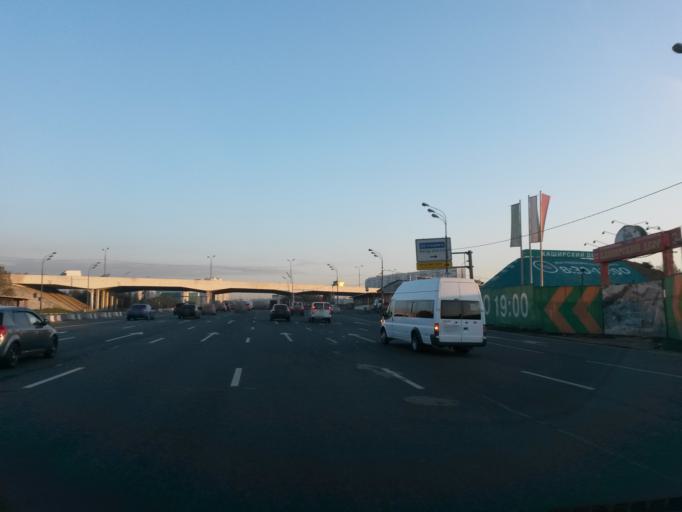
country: RU
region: Moscow
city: Annino
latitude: 55.5733
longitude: 37.5977
